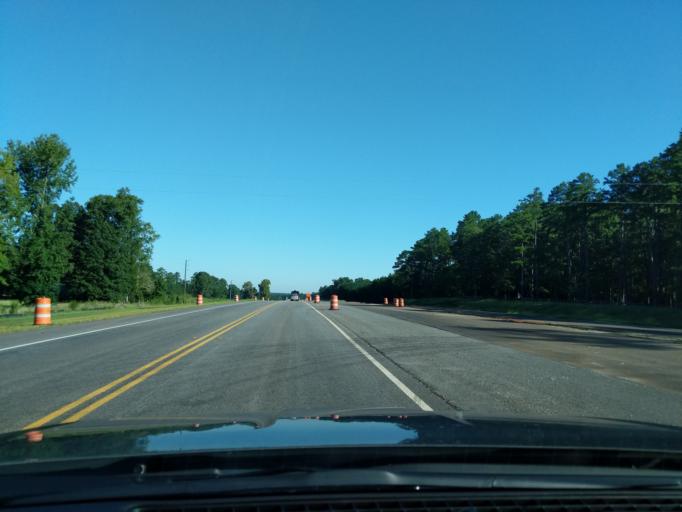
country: US
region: Georgia
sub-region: McDuffie County
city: Thomson
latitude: 33.5608
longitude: -82.5151
